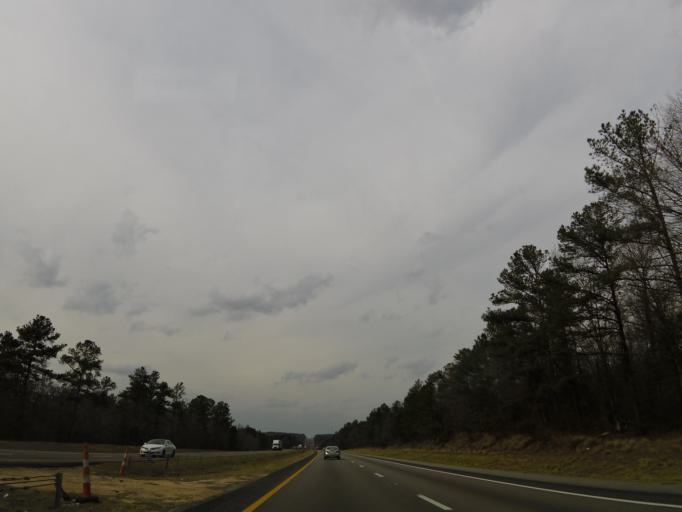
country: US
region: South Carolina
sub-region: Calhoun County
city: Oak Grove
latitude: 33.7120
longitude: -80.9208
